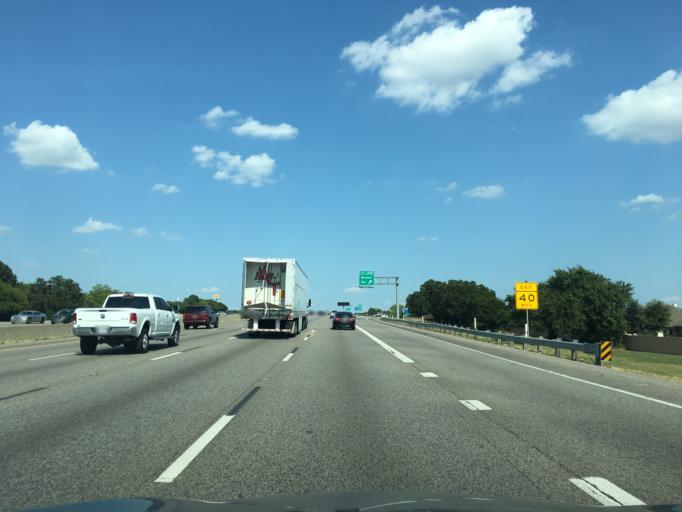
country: US
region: Texas
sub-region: Tarrant County
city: Dalworthington Gardens
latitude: 32.6745
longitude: -97.1558
